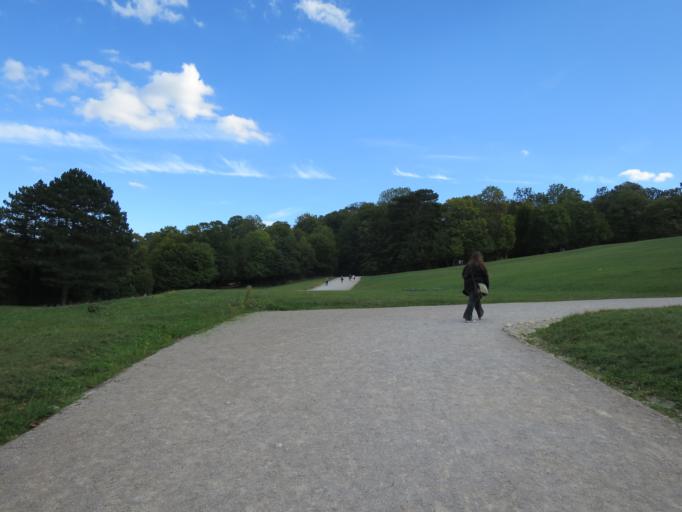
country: AT
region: Lower Austria
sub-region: Politischer Bezirk Modling
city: Vosendorf
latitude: 48.1811
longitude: 16.3096
